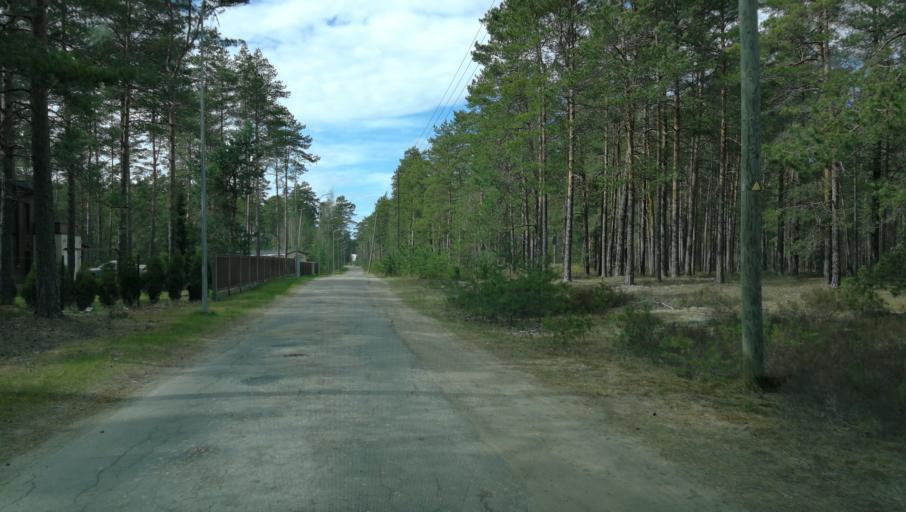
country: LV
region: Garkalne
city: Garkalne
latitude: 57.0382
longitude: 24.4411
